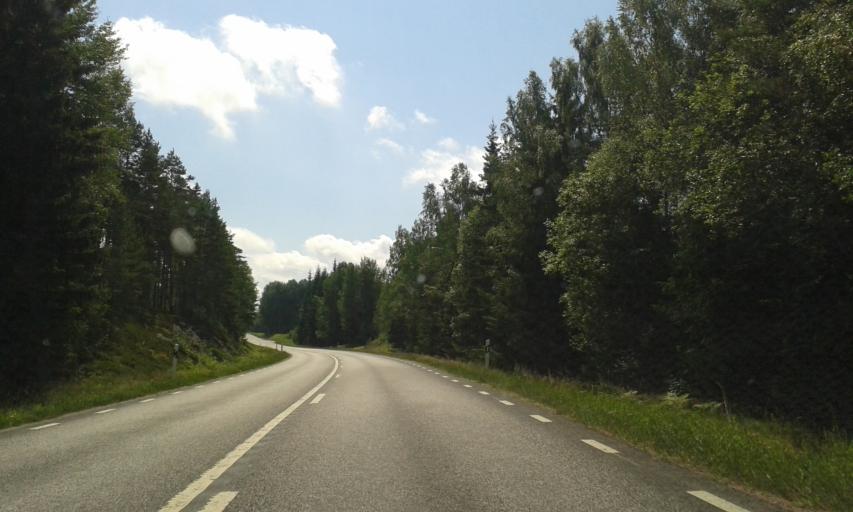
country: SE
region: Joenkoeping
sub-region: Varnamo Kommun
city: Bredaryd
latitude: 57.2023
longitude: 13.7097
